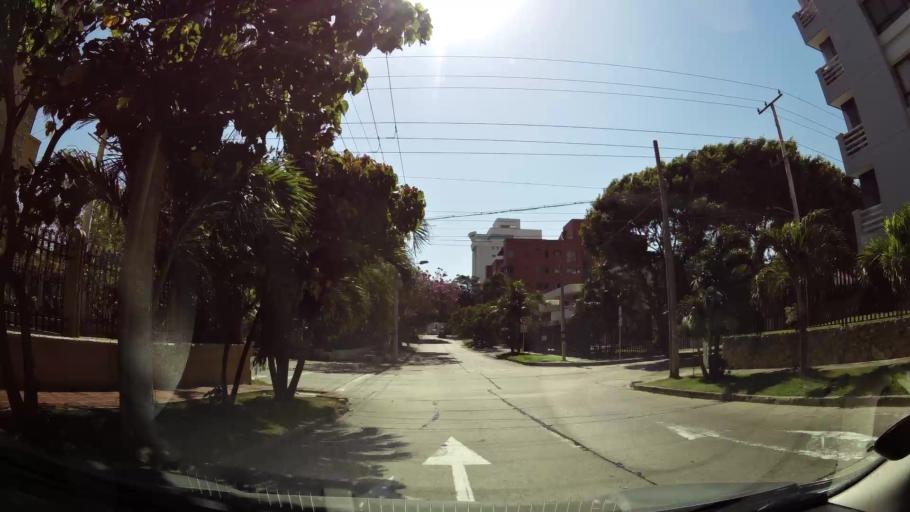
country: CO
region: Atlantico
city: Barranquilla
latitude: 11.0134
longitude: -74.8183
